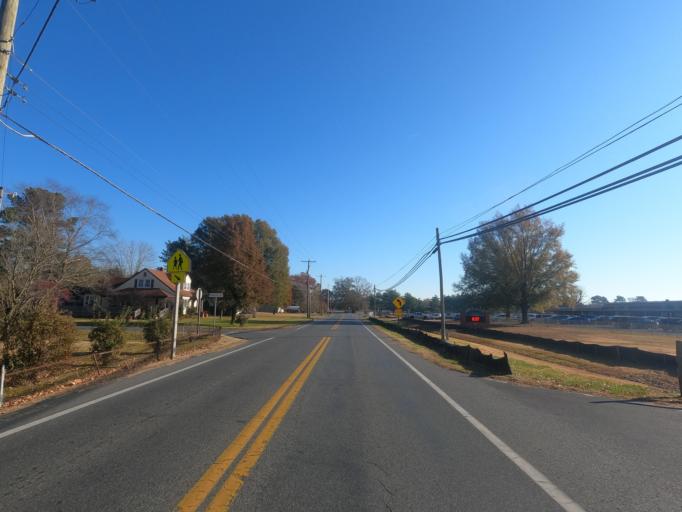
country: US
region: Maryland
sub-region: Wicomico County
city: Salisbury
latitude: 38.3778
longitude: -75.5210
